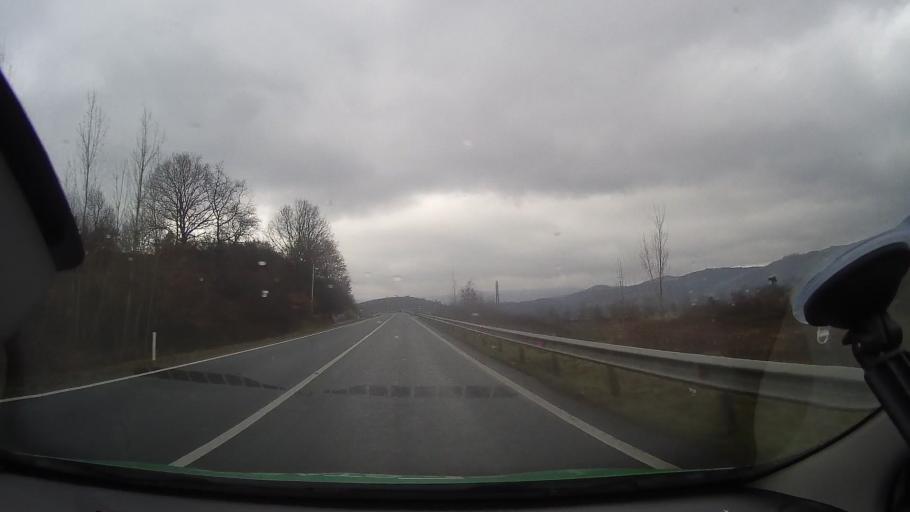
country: RO
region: Hunedoara
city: Vata de Jos
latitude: 46.2113
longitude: 22.5800
